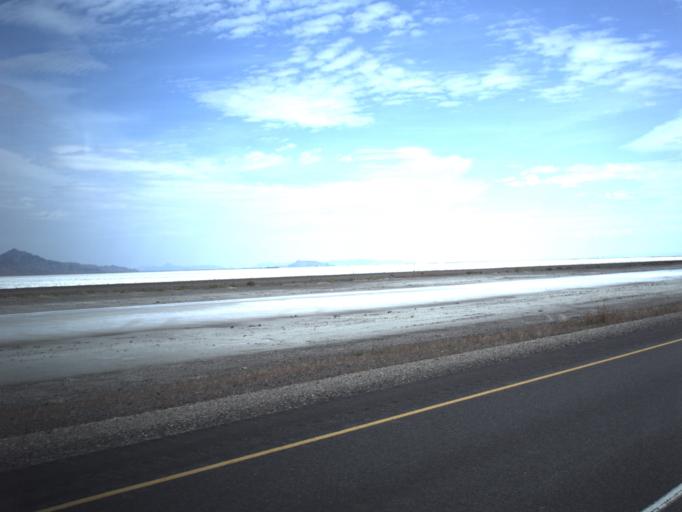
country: US
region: Utah
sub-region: Tooele County
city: Wendover
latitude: 40.7400
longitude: -113.9313
